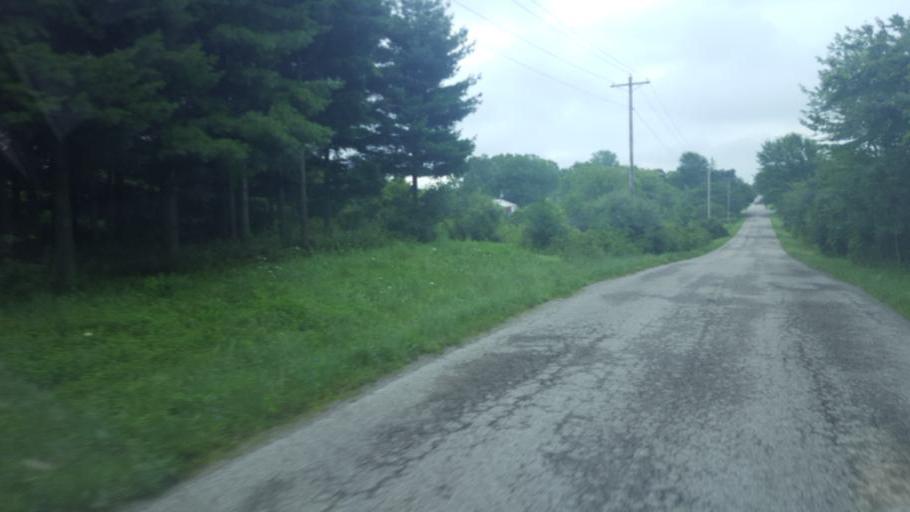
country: US
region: Ohio
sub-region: Knox County
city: Centerburg
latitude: 40.4213
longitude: -82.7259
